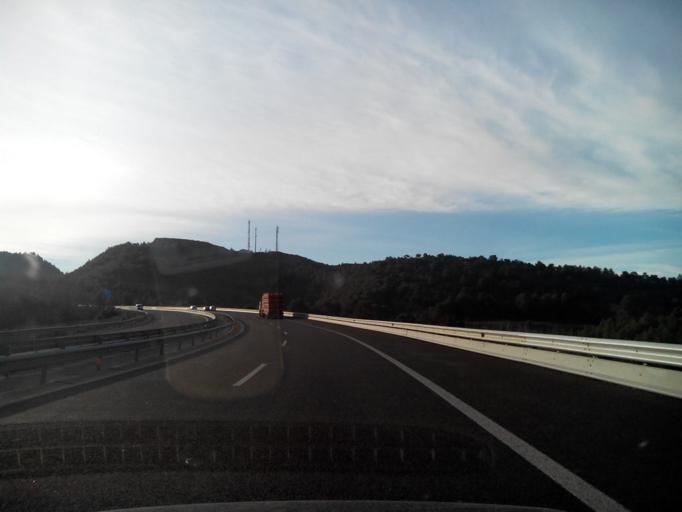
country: ES
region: Catalonia
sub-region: Provincia de Barcelona
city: Manresa
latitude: 41.6817
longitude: 1.8693
